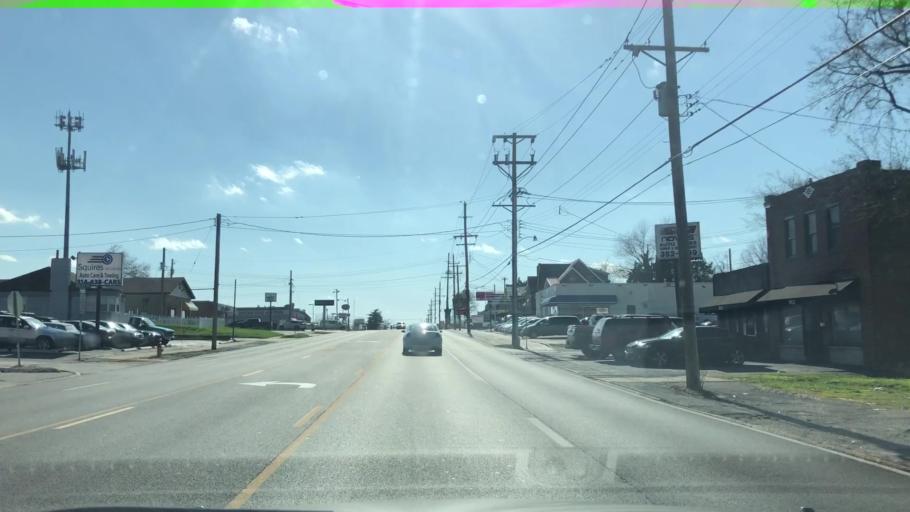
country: US
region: Missouri
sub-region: Saint Louis County
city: Saint George
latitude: 38.5561
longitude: -90.3108
